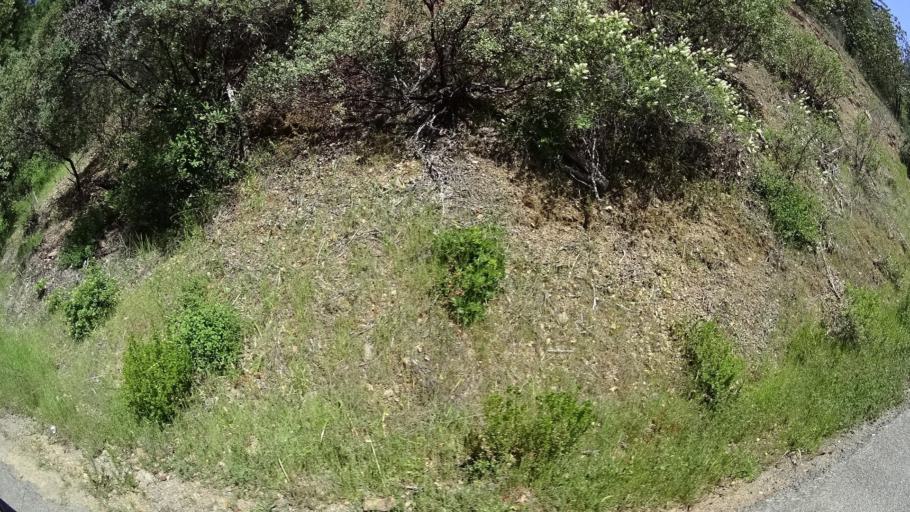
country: US
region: California
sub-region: Humboldt County
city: Redway
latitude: 40.1946
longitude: -123.5530
